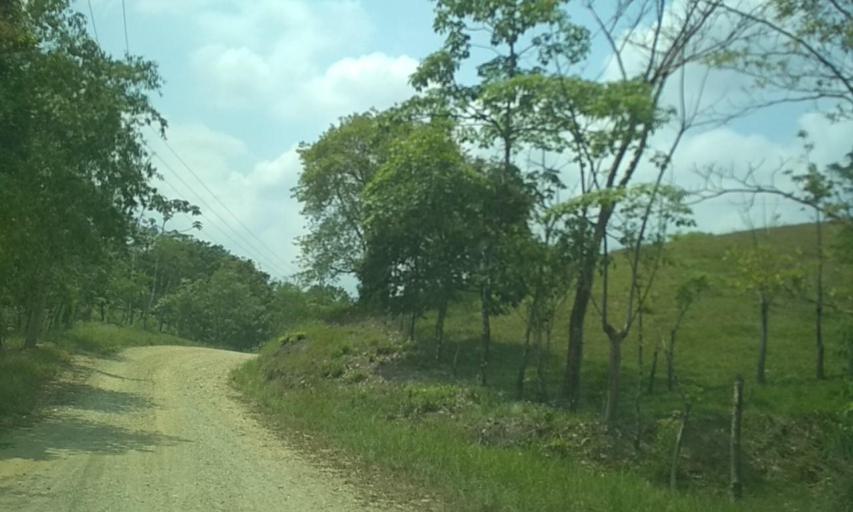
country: MX
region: Tabasco
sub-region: Huimanguillo
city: Francisco Rueda
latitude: 17.6154
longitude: -93.8130
